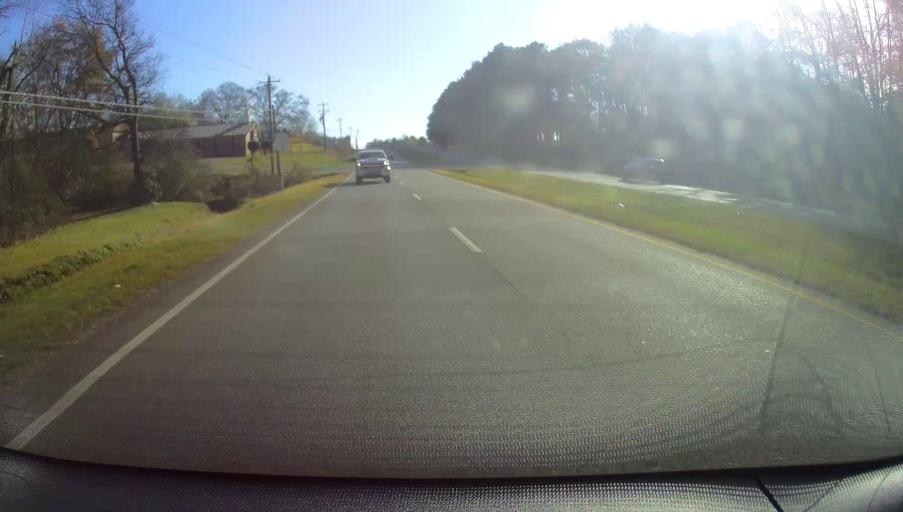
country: US
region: Alabama
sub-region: Limestone County
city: Athens
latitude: 34.7705
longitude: -86.9571
